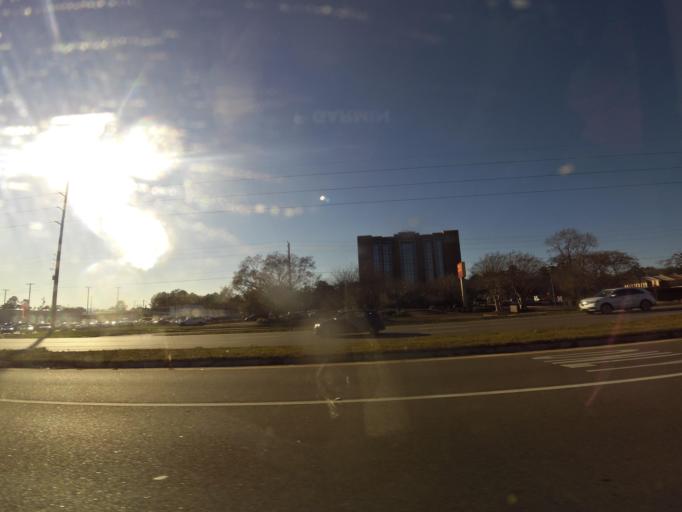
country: US
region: Alabama
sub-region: Houston County
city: Dothan
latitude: 31.2229
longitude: -85.4323
